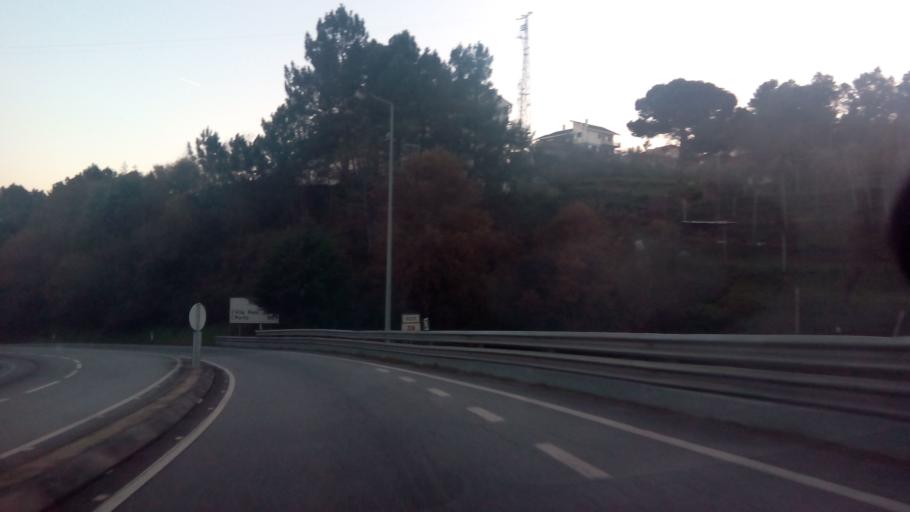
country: PT
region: Porto
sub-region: Amarante
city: Amarante
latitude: 41.2719
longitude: -8.0967
